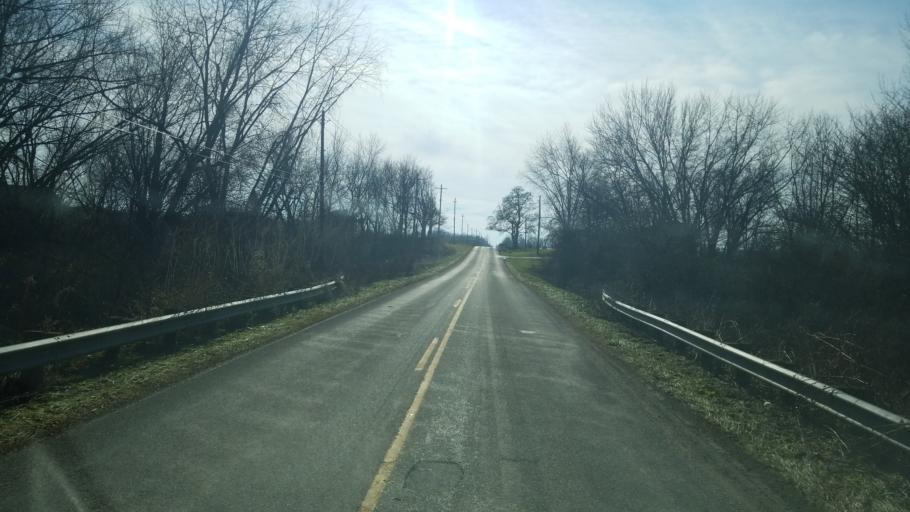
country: US
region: Ohio
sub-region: Ashtabula County
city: Roaming Shores
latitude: 41.6913
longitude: -80.8359
